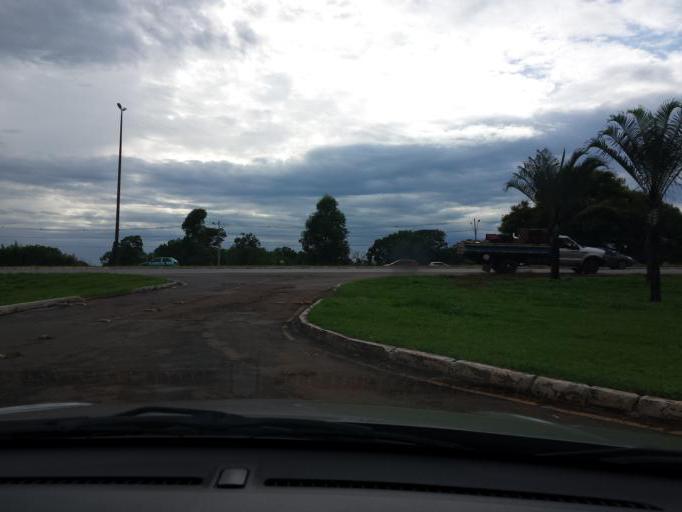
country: BR
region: Federal District
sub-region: Brasilia
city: Brasilia
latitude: -15.9214
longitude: -47.9749
